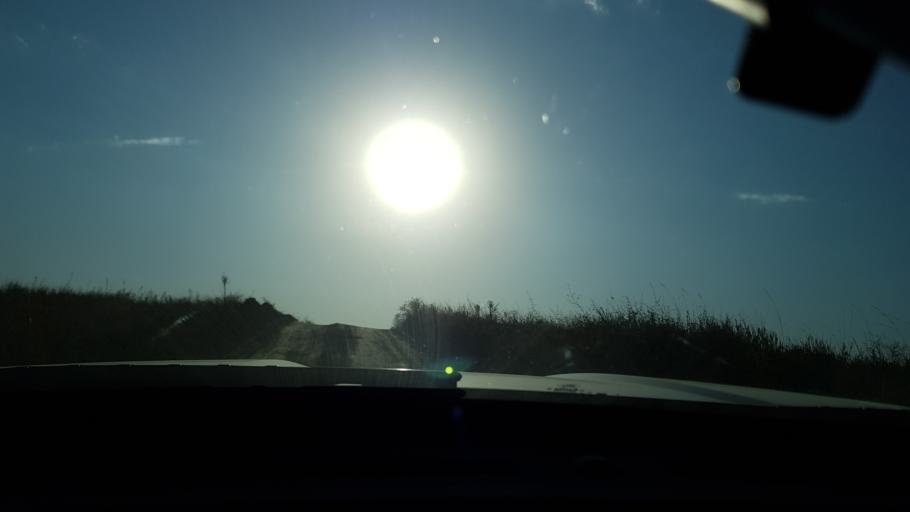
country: TM
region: Ahal
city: Baharly
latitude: 38.4099
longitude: 56.9158
